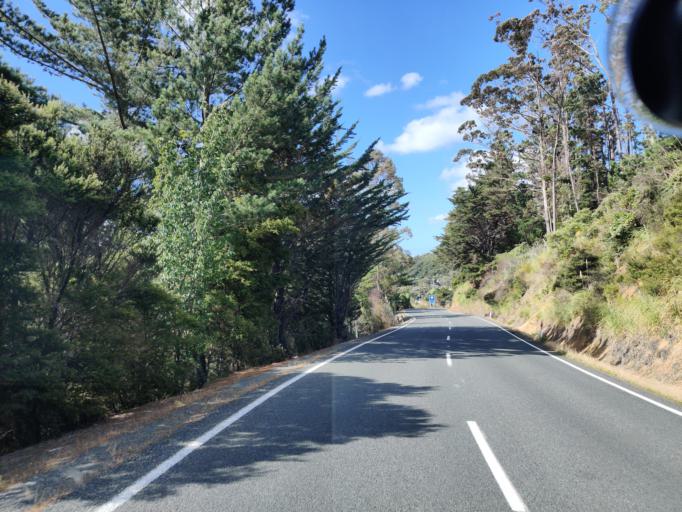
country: NZ
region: Northland
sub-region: Whangarei
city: Ngunguru
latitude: -35.6133
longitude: 174.5225
